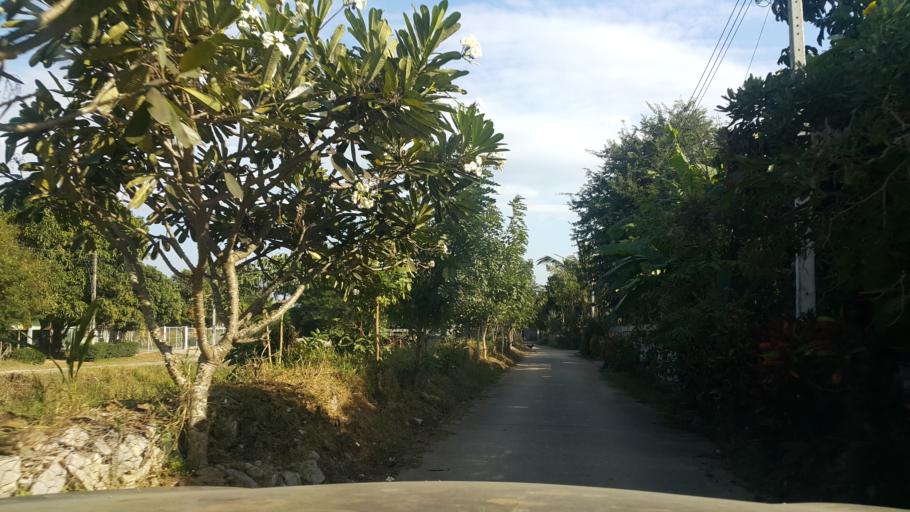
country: TH
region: Lampang
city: Hang Chat
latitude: 18.3137
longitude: 99.3509
